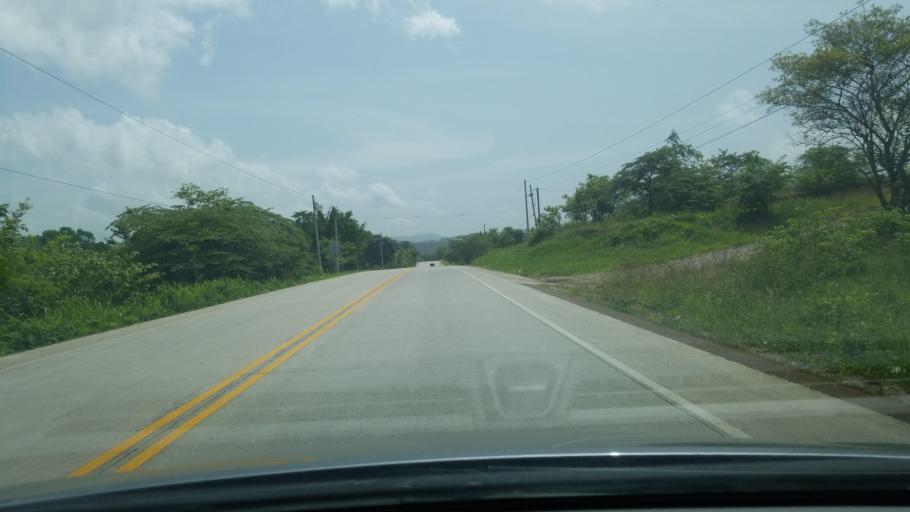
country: HN
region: Copan
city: Florida
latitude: 15.0614
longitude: -88.7936
